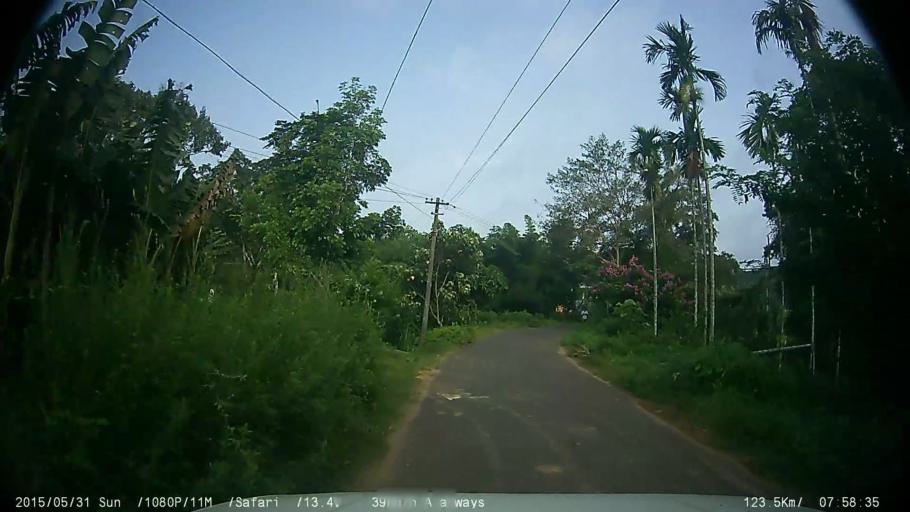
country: IN
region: Kerala
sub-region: Wayanad
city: Kalpetta
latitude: 11.6346
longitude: 76.0613
